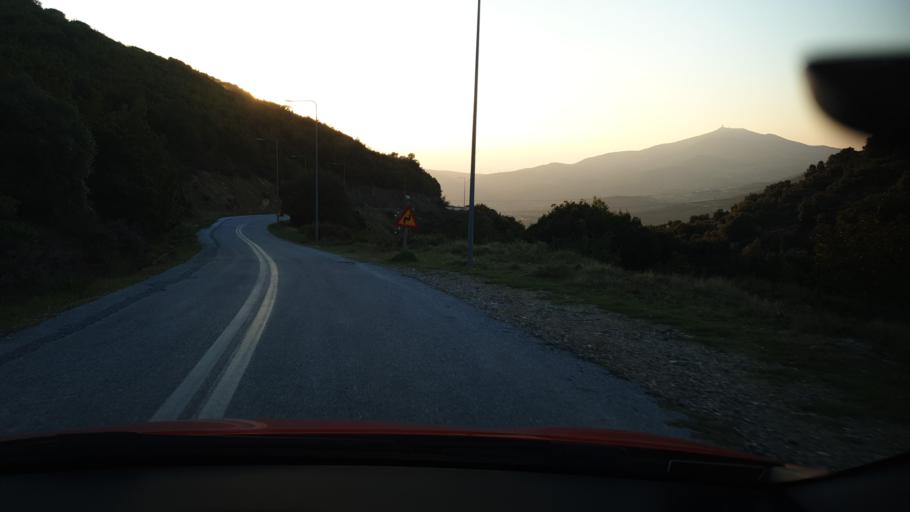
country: GR
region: Central Macedonia
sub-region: Nomos Thessalonikis
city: Peristera
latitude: 40.5207
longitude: 23.2073
